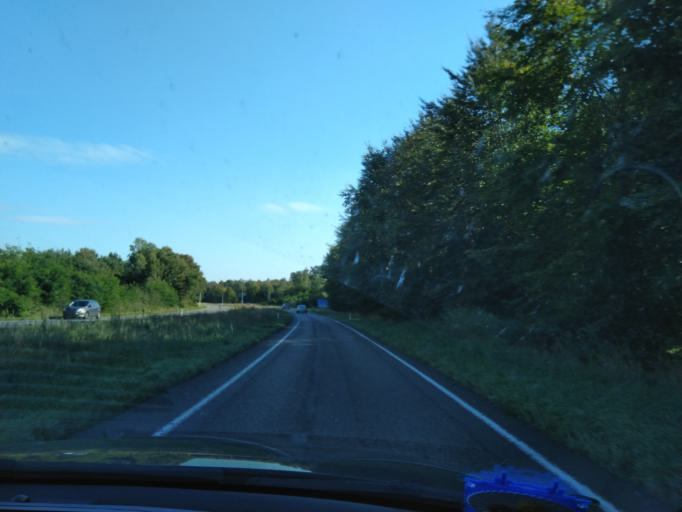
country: NL
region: Groningen
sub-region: Gemeente Veendam
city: Veendam
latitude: 53.0943
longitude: 6.9053
